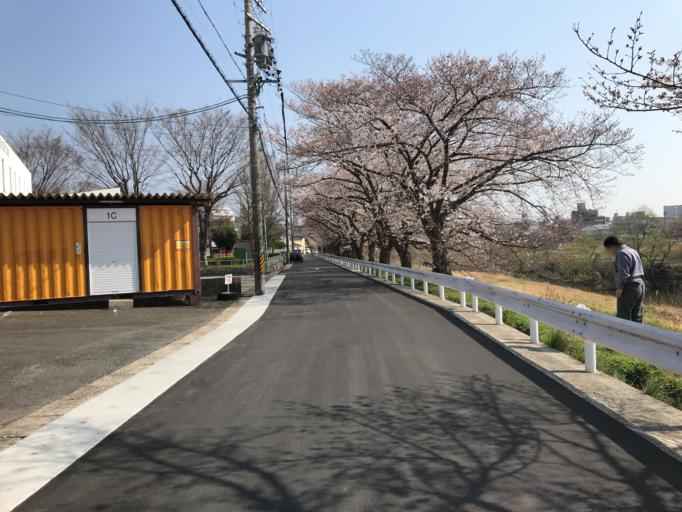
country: JP
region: Aichi
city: Nagoya-shi
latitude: 35.1255
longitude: 136.9801
